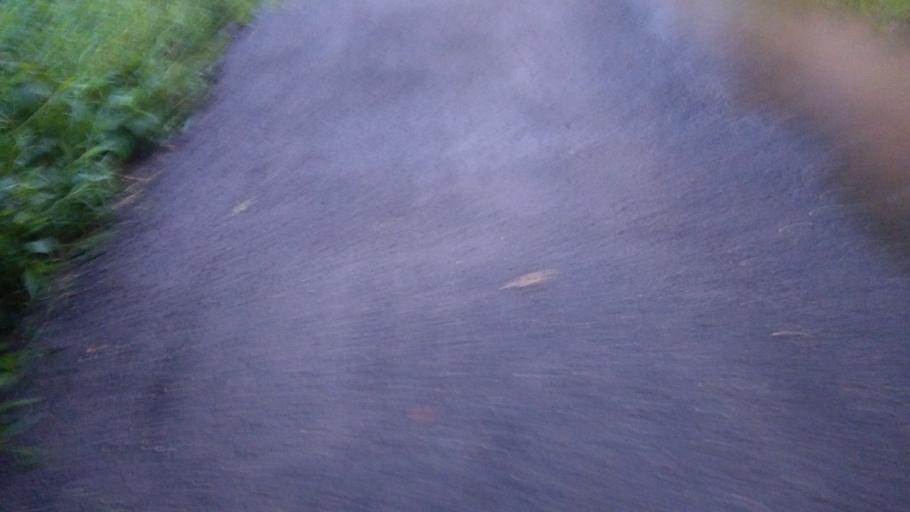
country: IN
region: Kerala
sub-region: Ernakulam
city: Ramamangalam
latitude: 9.9838
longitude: 76.4627
